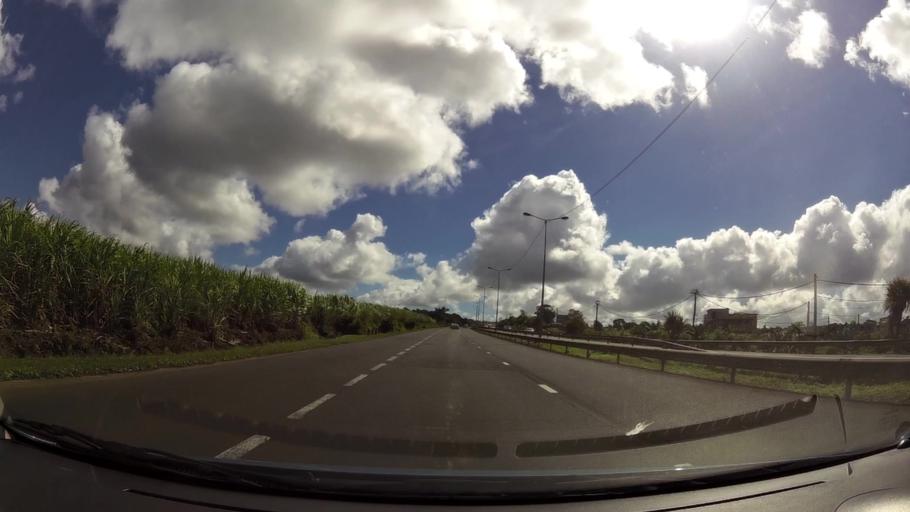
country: MU
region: Grand Port
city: Rose Belle
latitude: -20.3946
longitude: 57.5788
